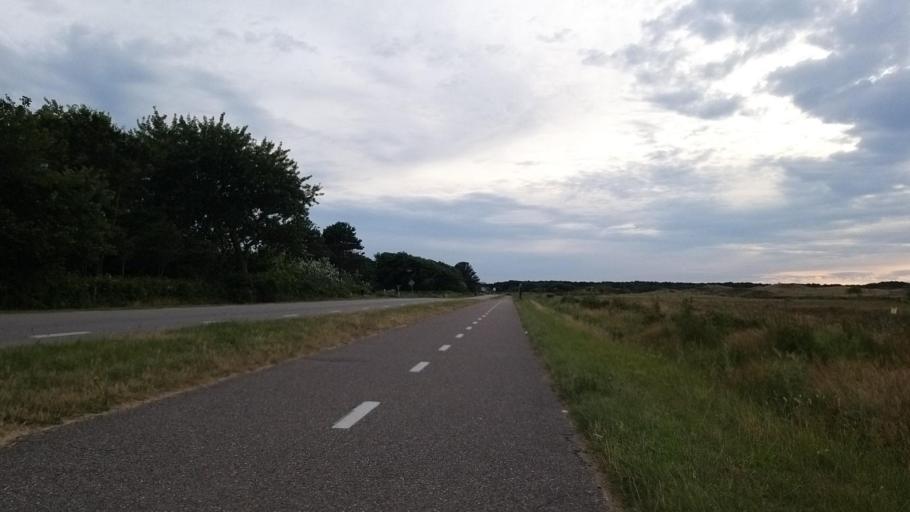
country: NL
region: North Holland
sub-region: Gemeente Texel
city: Den Burg
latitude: 53.1054
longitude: 4.7839
